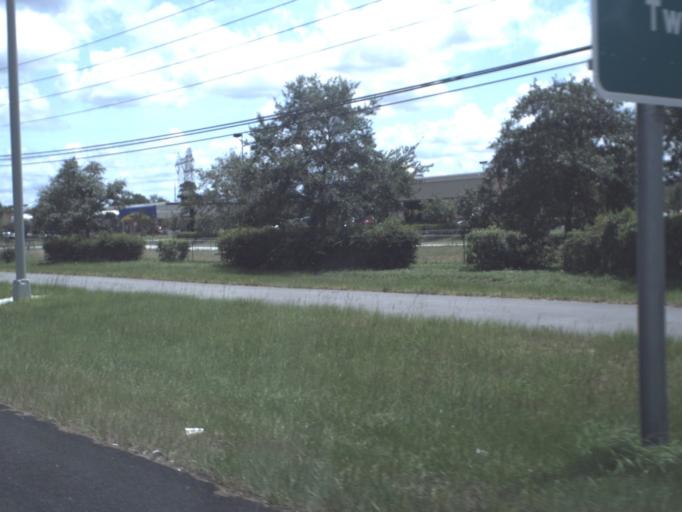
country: US
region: Florida
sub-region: Hernando County
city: Brookridge
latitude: 28.5336
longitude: -82.5041
